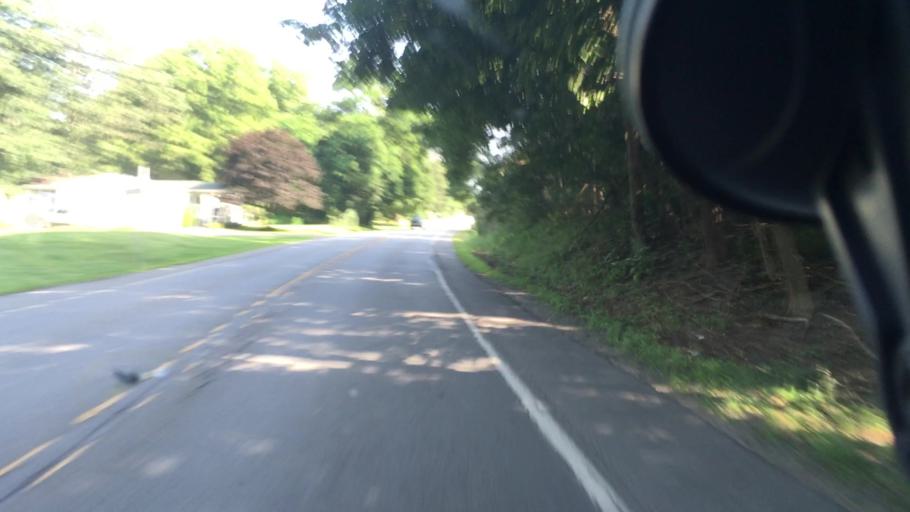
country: US
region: Pennsylvania
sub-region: Butler County
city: Slippery Rock
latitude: 41.0282
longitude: -80.1908
